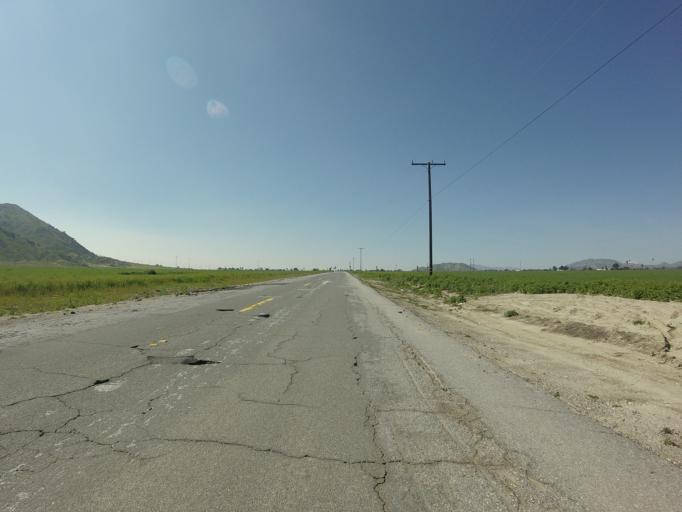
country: US
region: California
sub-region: Riverside County
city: Lakeview
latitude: 33.9195
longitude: -117.1343
